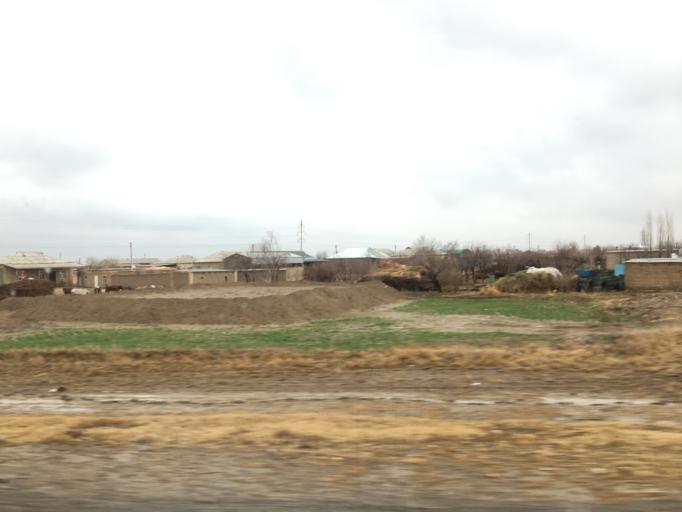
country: TM
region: Mary
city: Yoloeten
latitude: 37.3091
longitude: 62.3206
